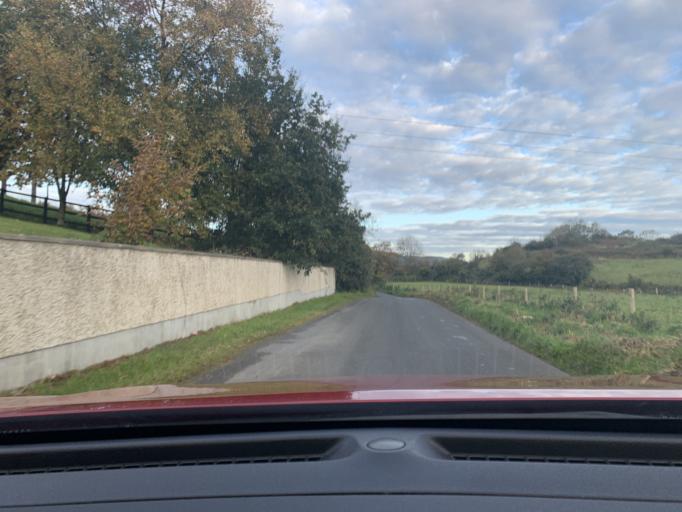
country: IE
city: Ballisodare
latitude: 54.2171
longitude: -8.4972
